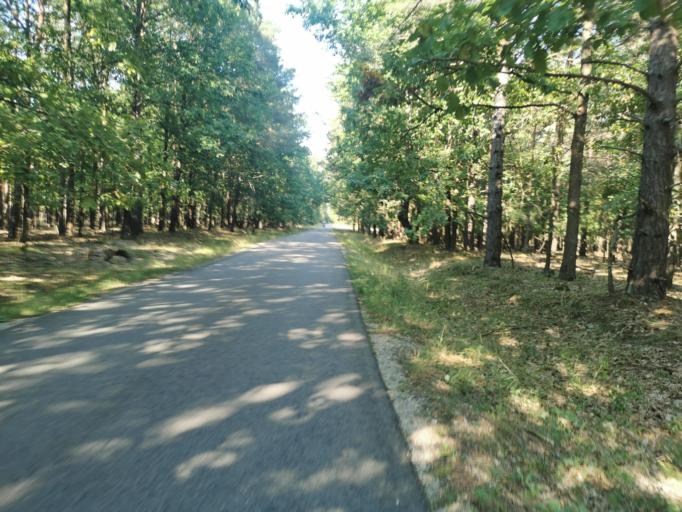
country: SK
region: Trnavsky
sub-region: Okres Senica
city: Senica
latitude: 48.6400
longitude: 17.2643
